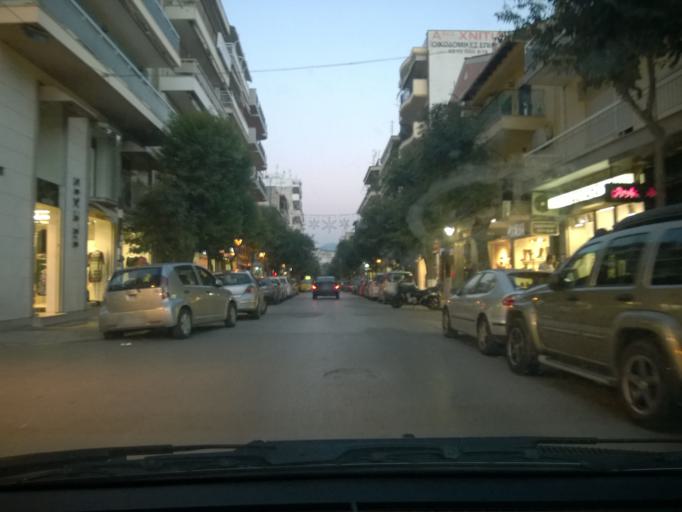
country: GR
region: Central Macedonia
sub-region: Nomos Thessalonikis
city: Ampelokipoi
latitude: 40.6525
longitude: 22.9228
